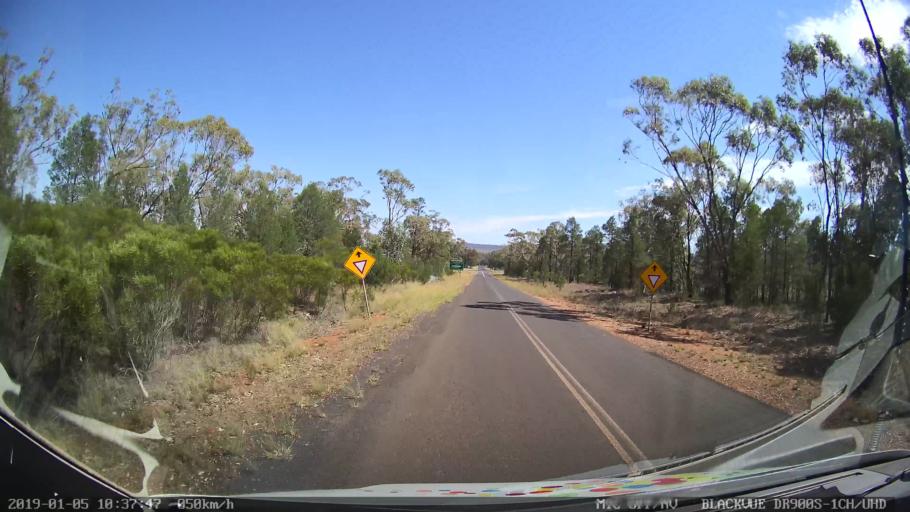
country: AU
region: New South Wales
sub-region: Gilgandra
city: Gilgandra
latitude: -31.4722
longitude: 148.9207
